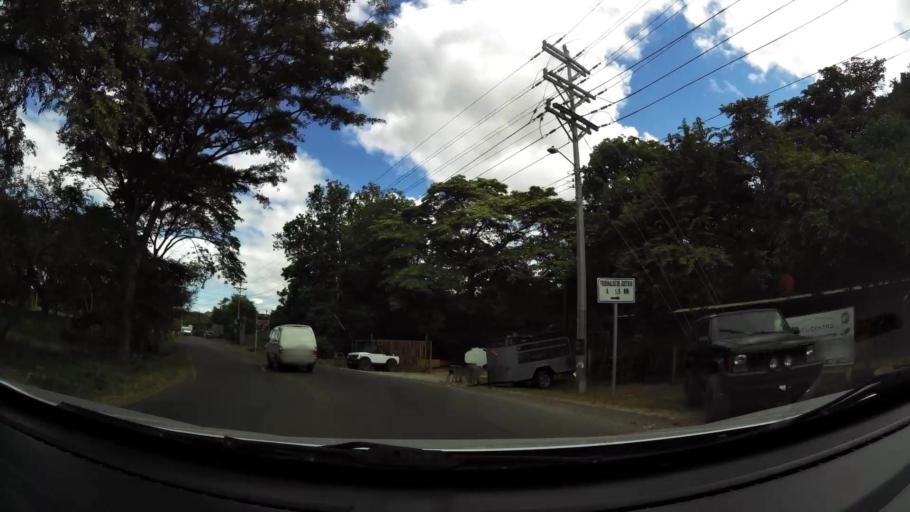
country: CR
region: Guanacaste
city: Santa Cruz
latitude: 10.2701
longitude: -85.5902
